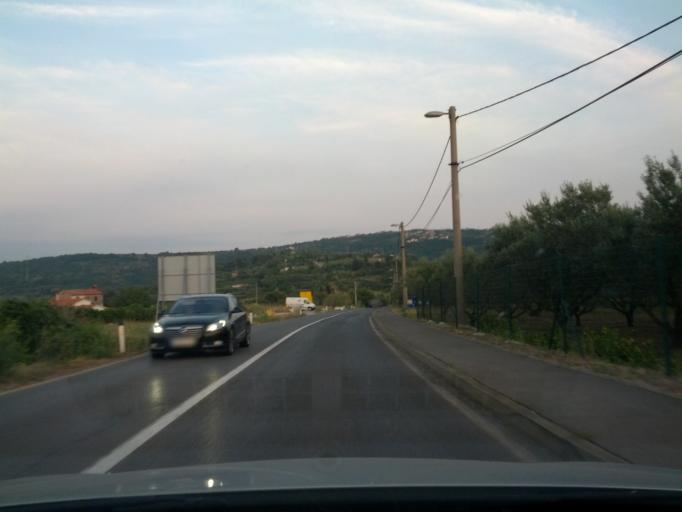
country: SI
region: Izola-Isola
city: Jagodje
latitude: 45.5285
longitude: 13.6394
